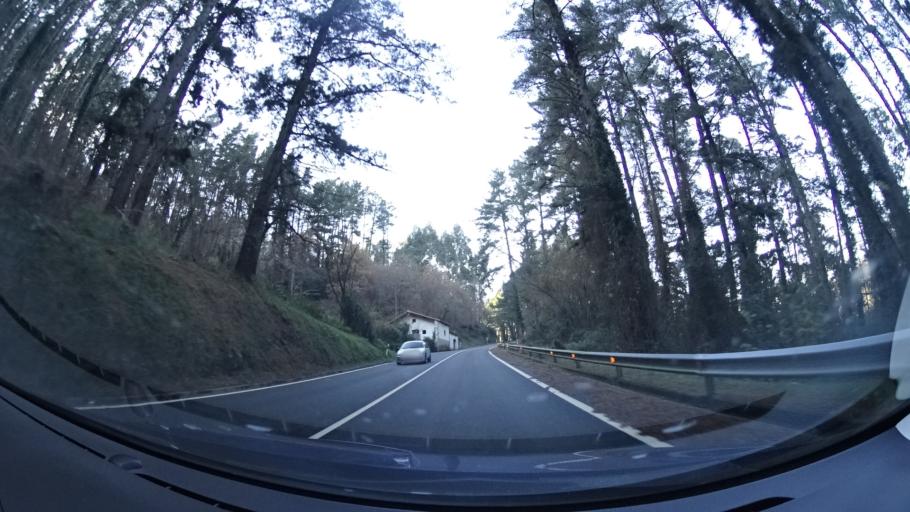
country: ES
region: Basque Country
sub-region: Bizkaia
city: Bakio
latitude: 43.3820
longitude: -2.7753
